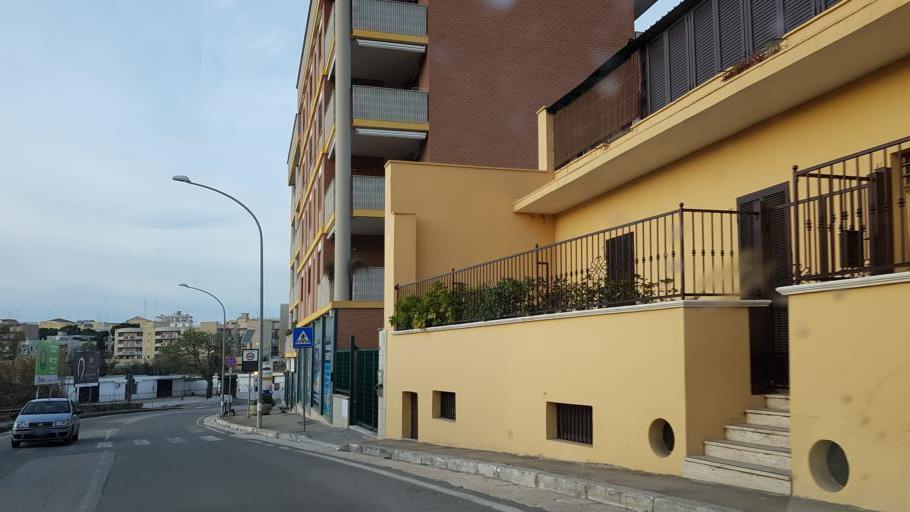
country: IT
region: Apulia
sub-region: Provincia di Brindisi
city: Brindisi
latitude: 40.6295
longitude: 17.9465
